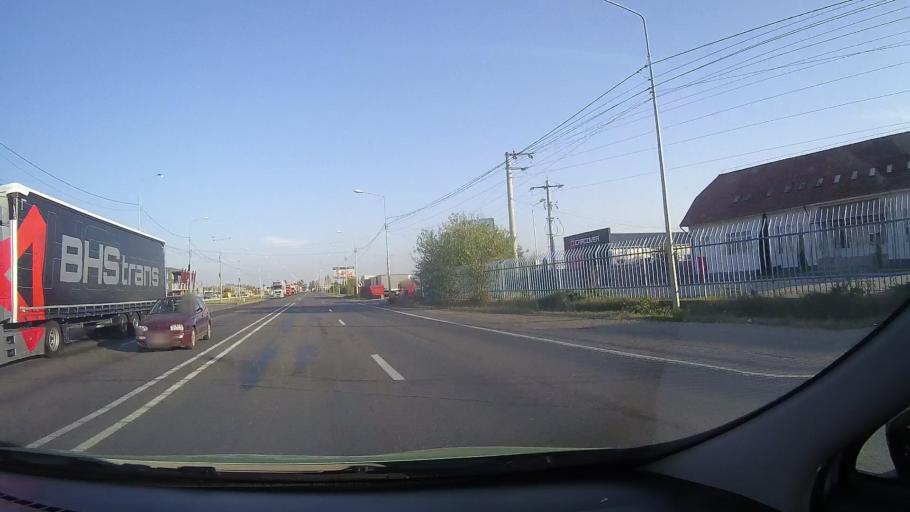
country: RO
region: Bihor
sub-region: Comuna Bors
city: Santion
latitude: 47.1051
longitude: 21.8300
